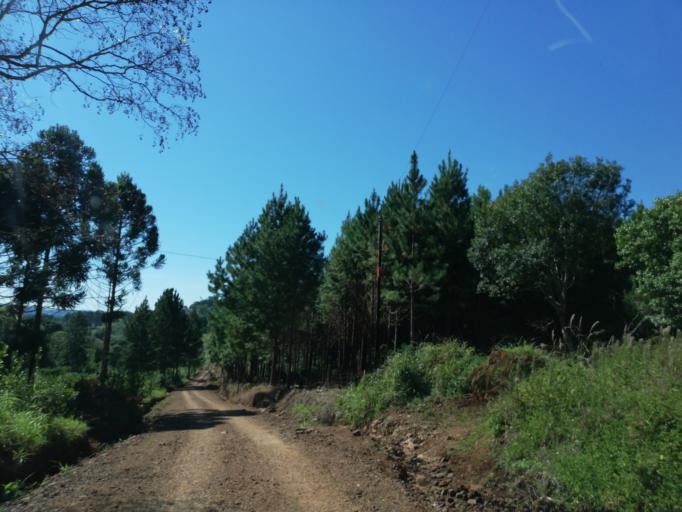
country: AR
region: Misiones
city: Dos de Mayo
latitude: -27.0717
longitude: -54.3939
